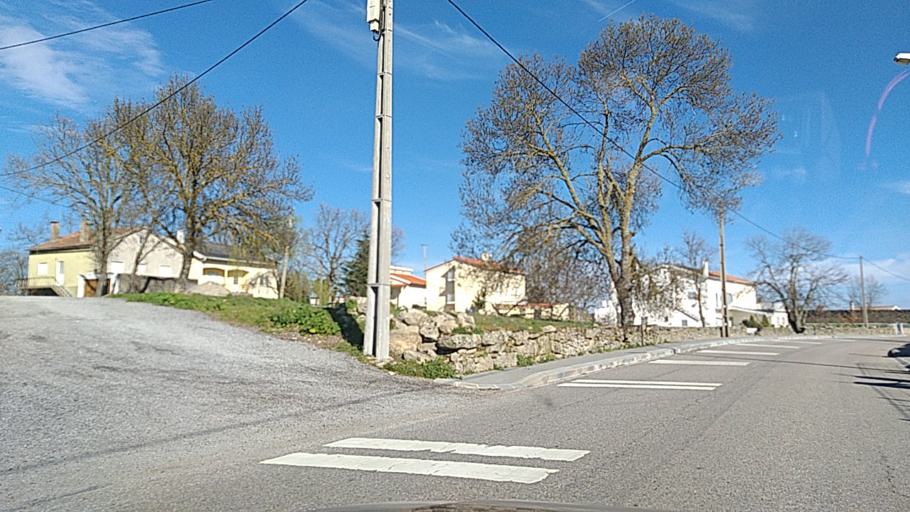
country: PT
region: Guarda
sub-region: Guarda
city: Sequeira
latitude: 40.6016
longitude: -7.0614
